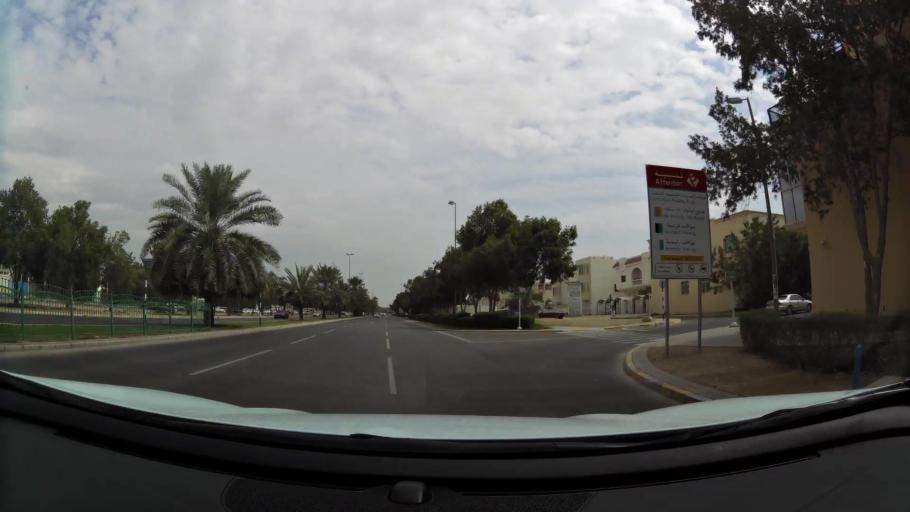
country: AE
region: Abu Dhabi
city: Al Ain
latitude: 24.2135
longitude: 55.7819
